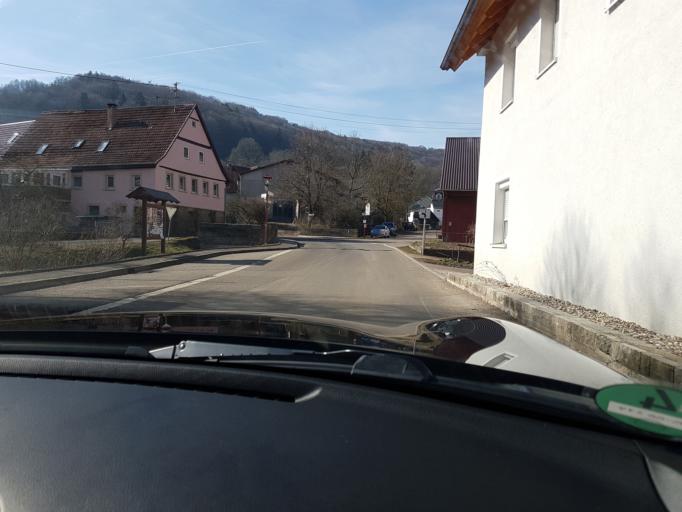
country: DE
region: Baden-Wuerttemberg
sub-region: Regierungsbezirk Stuttgart
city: Mulfingen
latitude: 49.3150
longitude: 9.8048
